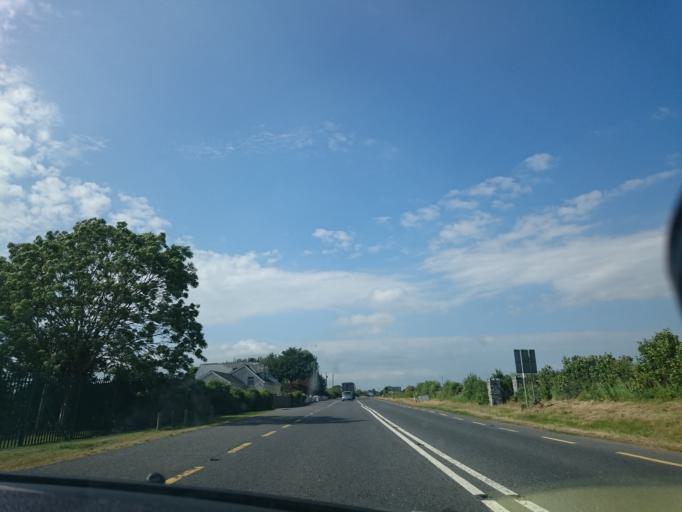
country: IE
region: Leinster
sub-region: Kilkenny
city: Kilkenny
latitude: 52.5843
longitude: -7.2396
